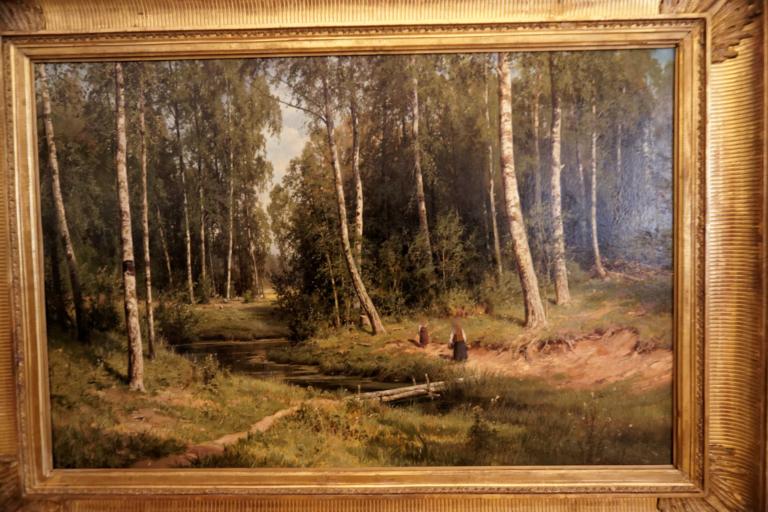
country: RU
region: St.-Petersburg
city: Saint Petersburg
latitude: 59.9386
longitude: 30.3330
